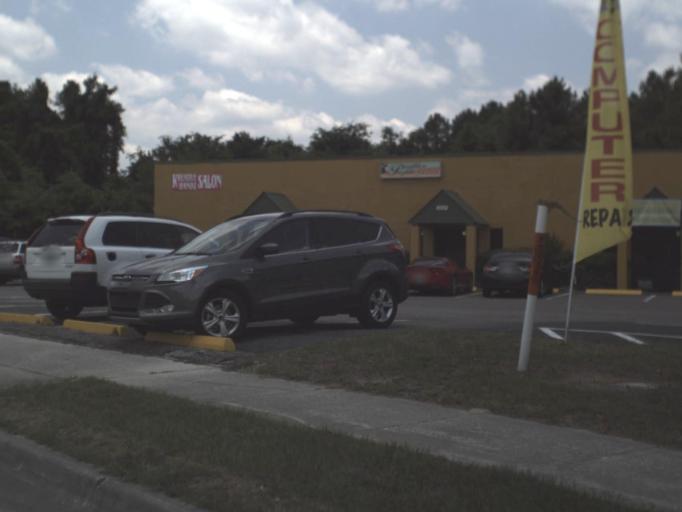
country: US
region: Florida
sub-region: Duval County
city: Jacksonville
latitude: 30.3785
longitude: -81.7091
